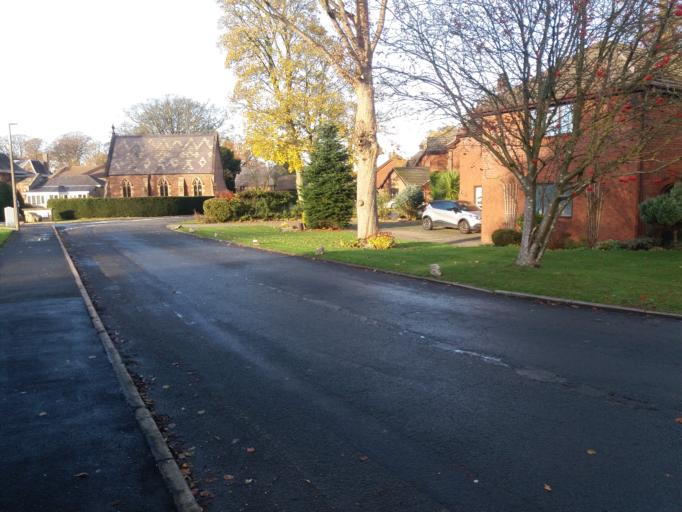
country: GB
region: England
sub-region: Lancashire
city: Euxton
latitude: 53.6600
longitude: -2.6753
